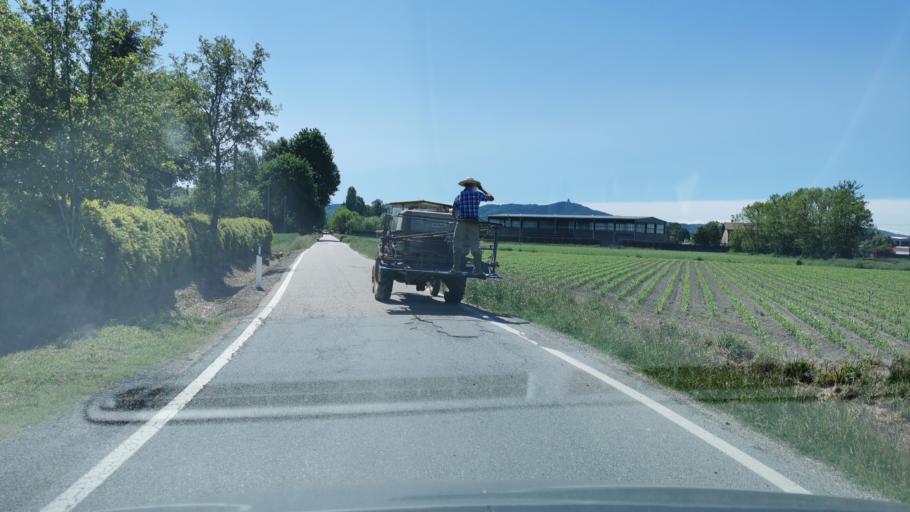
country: IT
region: Piedmont
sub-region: Provincia di Torino
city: Settimo Torinese
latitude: 45.1602
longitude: 7.7439
